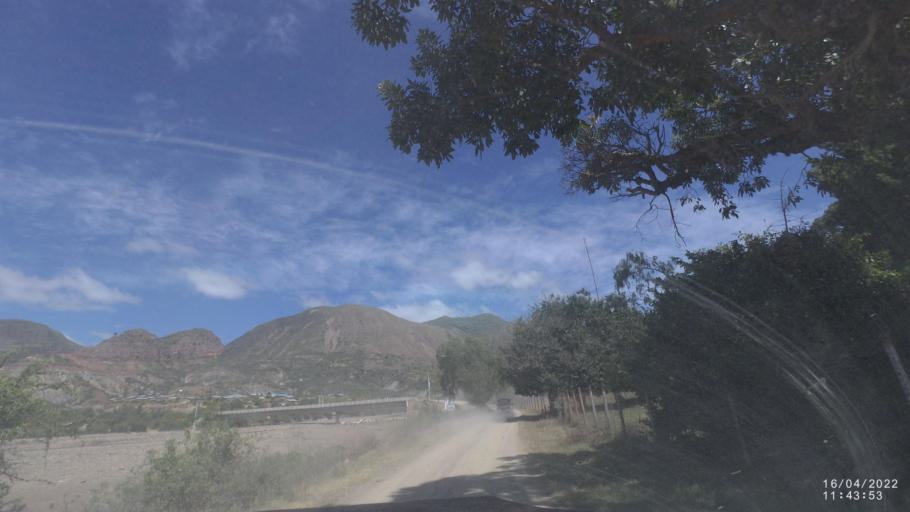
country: BO
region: Cochabamba
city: Mizque
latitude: -17.9823
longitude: -65.6307
